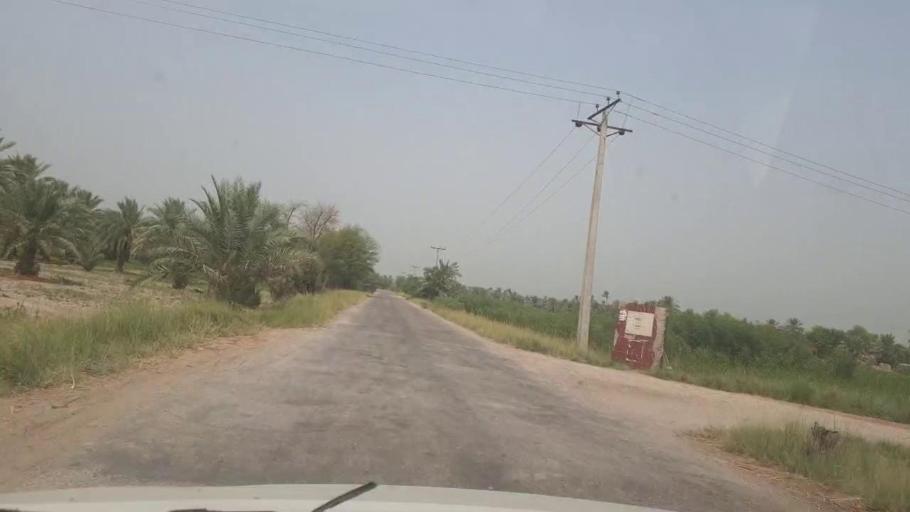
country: PK
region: Sindh
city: Kot Diji
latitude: 27.3624
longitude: 68.6853
